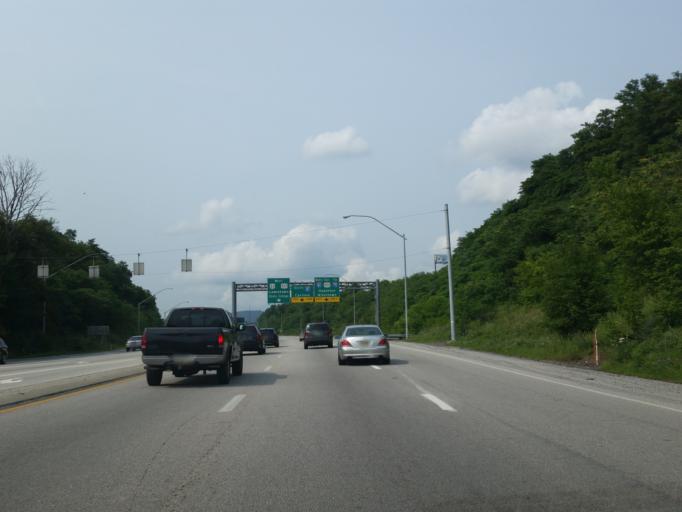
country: US
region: Pennsylvania
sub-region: Dauphin County
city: Harrisburg
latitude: 40.2915
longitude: -76.8816
